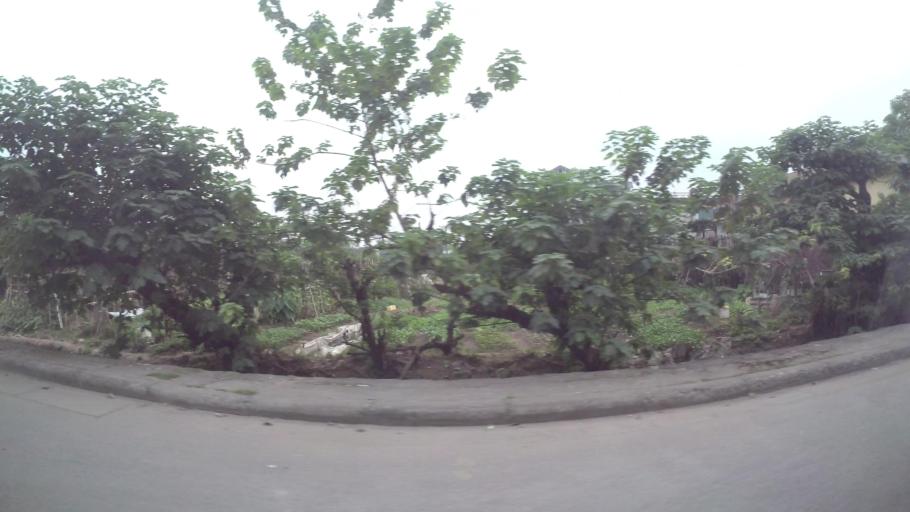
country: VN
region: Ha Noi
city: Hoan Kiem
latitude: 21.0660
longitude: 105.8854
